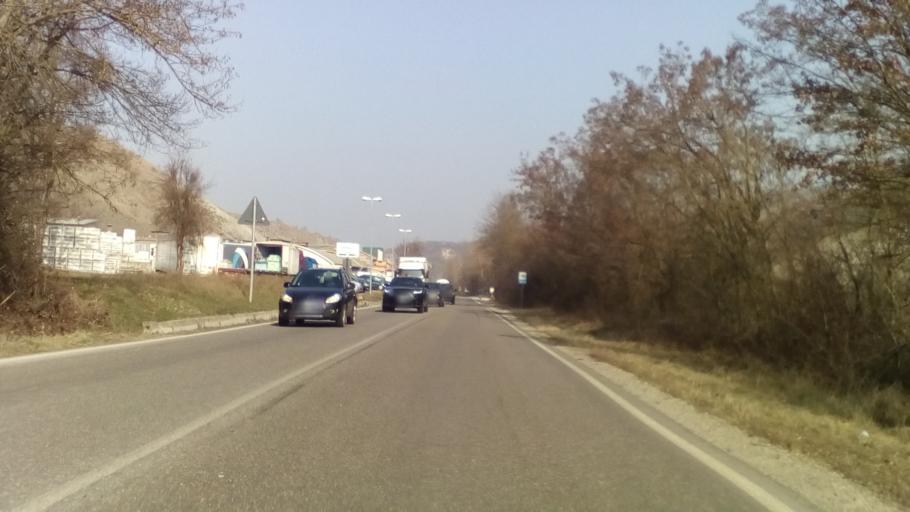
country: IT
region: Emilia-Romagna
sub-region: Provincia di Modena
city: Gorzano
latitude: 44.4678
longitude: 10.8401
